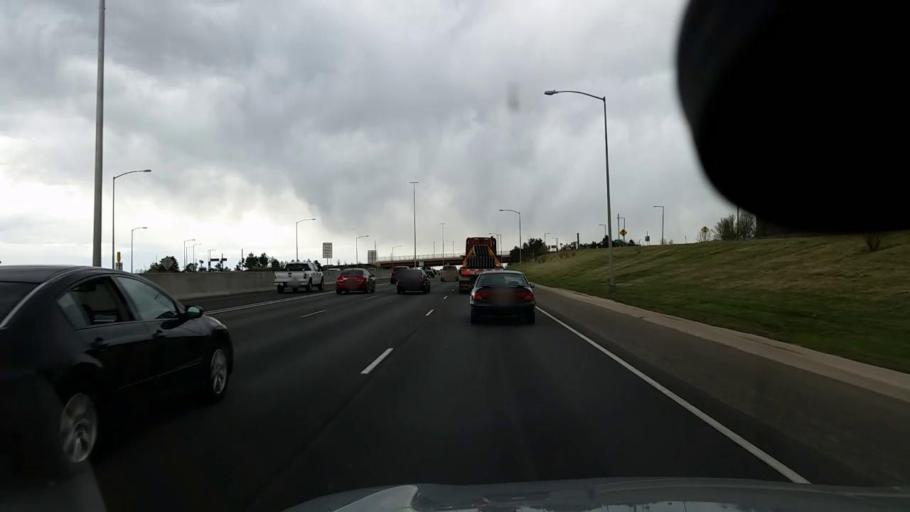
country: US
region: Colorado
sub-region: Adams County
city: Thornton
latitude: 39.8647
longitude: -104.9874
